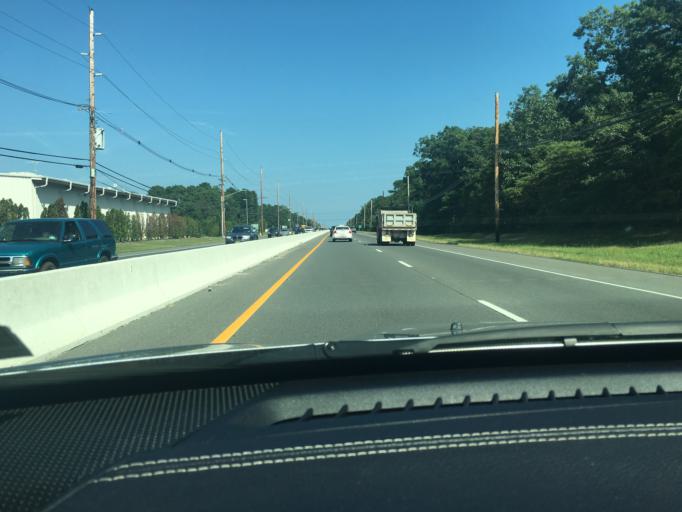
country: US
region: New Jersey
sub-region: Ocean County
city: Leisure Village
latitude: 40.0519
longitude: -74.1866
